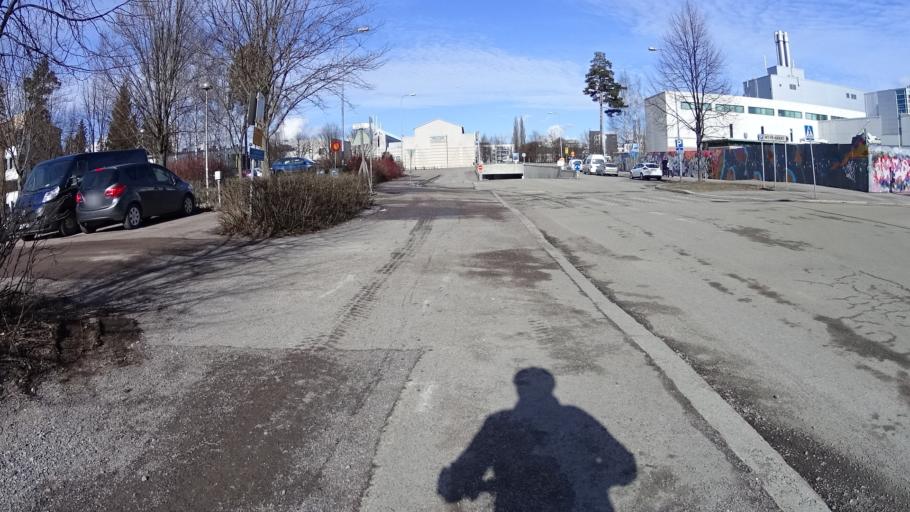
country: FI
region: Uusimaa
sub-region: Helsinki
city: Teekkarikylae
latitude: 60.2599
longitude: 24.8511
